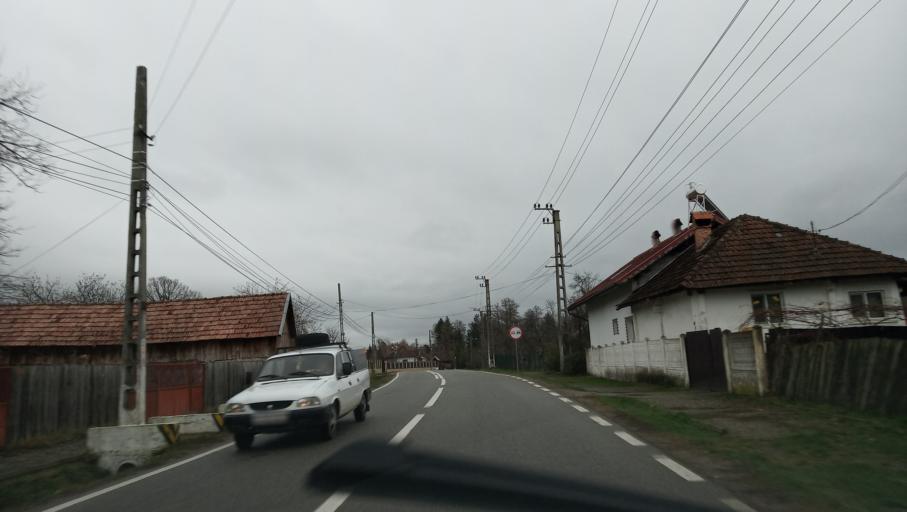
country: RO
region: Gorj
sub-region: Novaci
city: Pociovalistea
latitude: 45.1534
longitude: 23.6412
